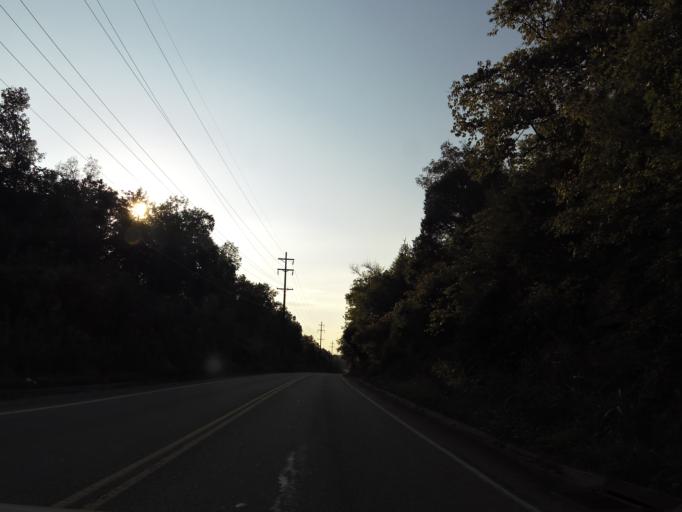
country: US
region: Tennessee
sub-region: Knox County
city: Mascot
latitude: 36.0649
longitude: -83.7132
